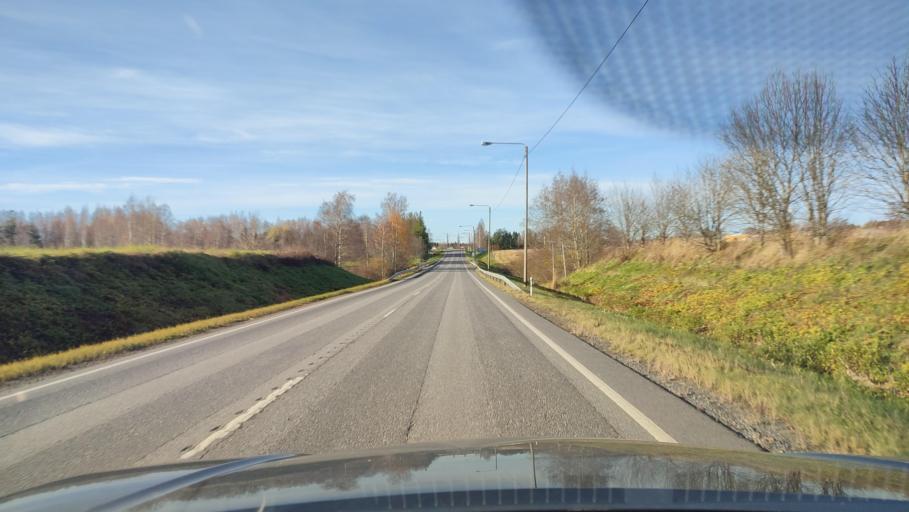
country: FI
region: Southern Ostrobothnia
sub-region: Suupohja
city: Teuva
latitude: 62.4915
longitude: 21.7579
